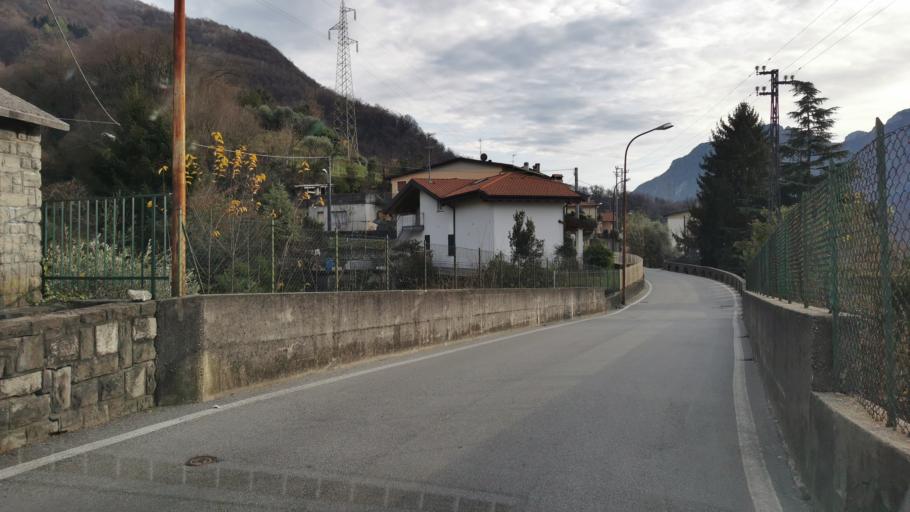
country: IT
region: Lombardy
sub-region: Provincia di Lecco
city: Mandello del Lario
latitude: 45.9248
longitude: 9.3265
